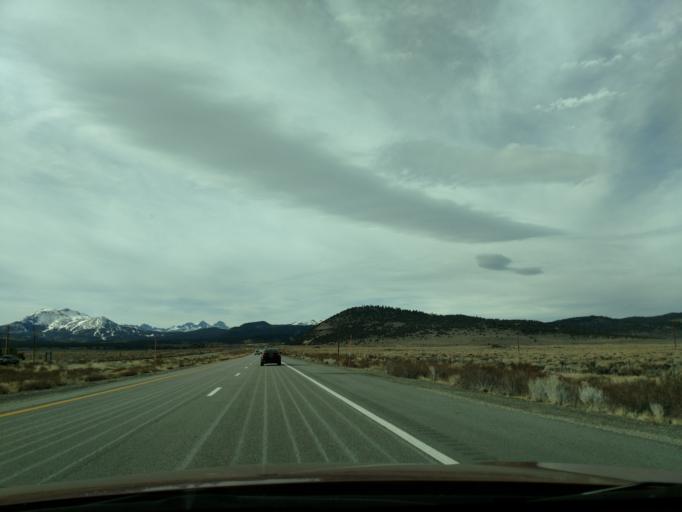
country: US
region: California
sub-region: Mono County
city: Mammoth Lakes
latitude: 37.6295
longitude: -118.8654
